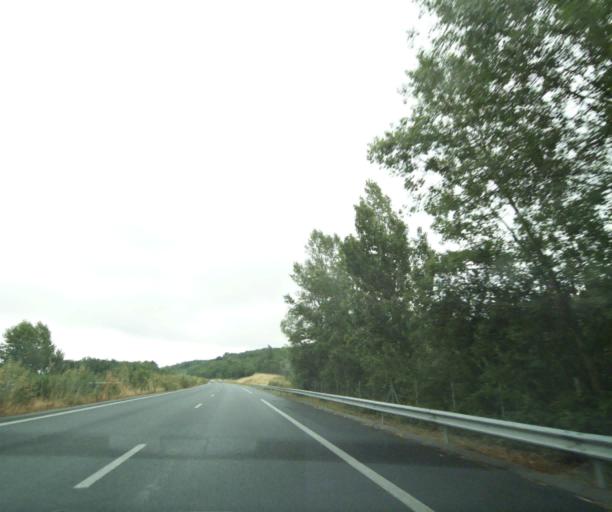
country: FR
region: Midi-Pyrenees
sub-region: Departement du Tarn
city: Lagrave
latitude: 43.8849
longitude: 1.9951
